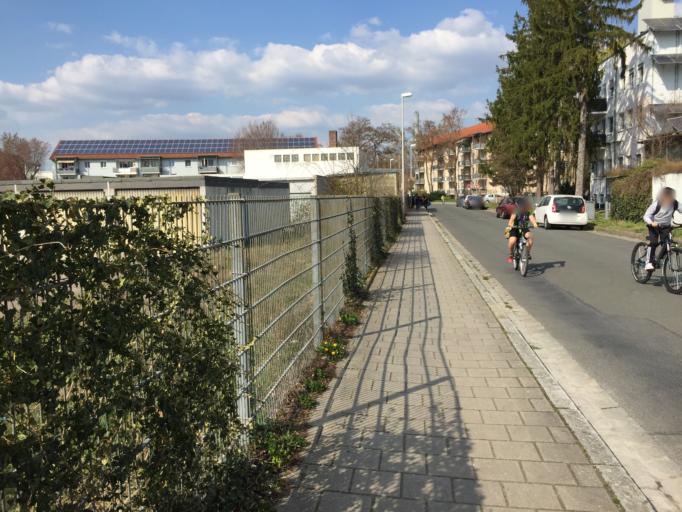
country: DE
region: Bavaria
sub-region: Regierungsbezirk Mittelfranken
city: Erlangen
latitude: 49.5836
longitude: 10.9989
